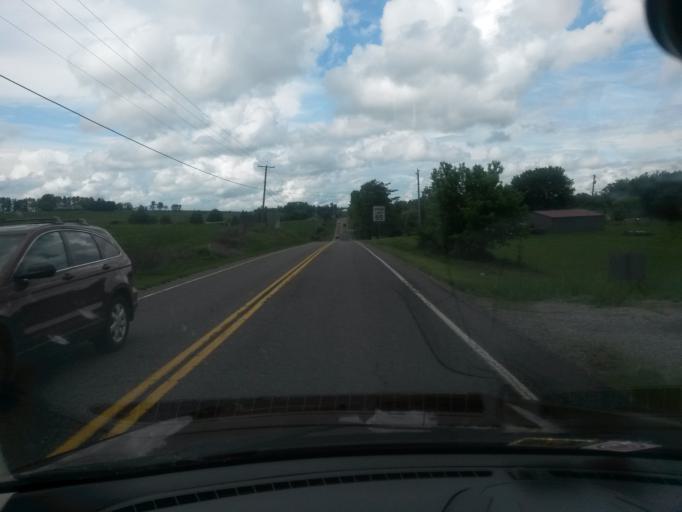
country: US
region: Virginia
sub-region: Montgomery County
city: Christiansburg
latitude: 37.0826
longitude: -80.4523
